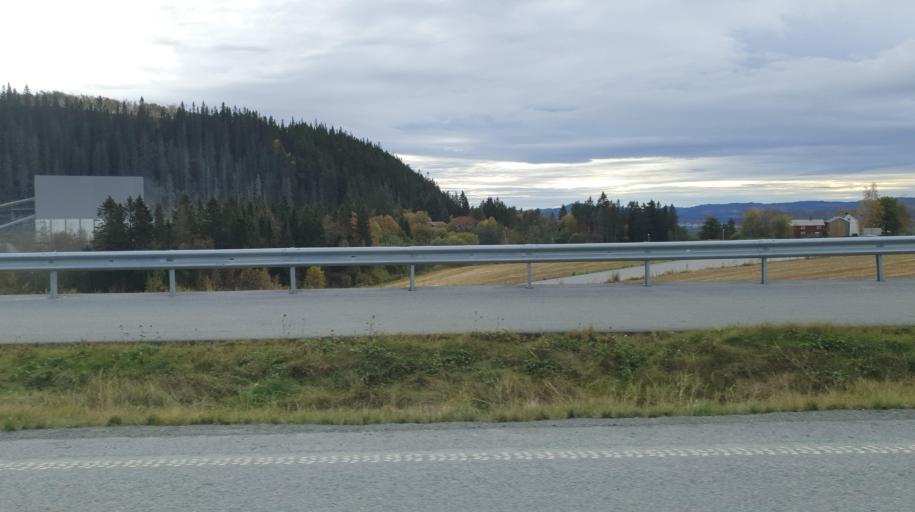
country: NO
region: Sor-Trondelag
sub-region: Klaebu
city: Klaebu
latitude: 63.3219
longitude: 10.3789
